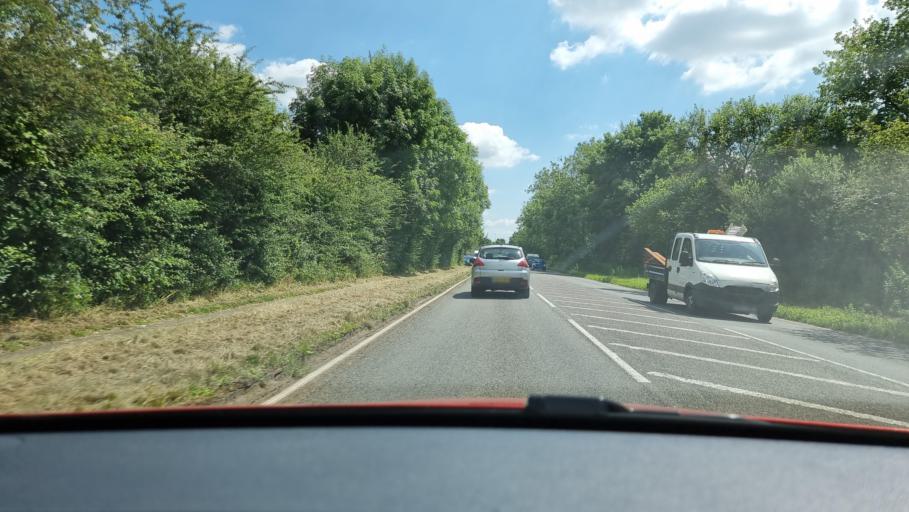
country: GB
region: England
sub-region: Oxfordshire
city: Kidlington
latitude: 51.8345
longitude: -1.3041
